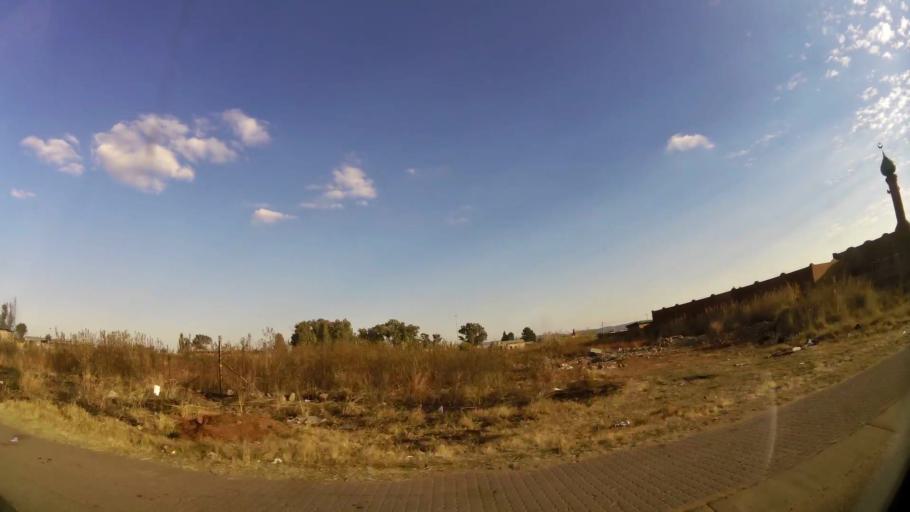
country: ZA
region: Gauteng
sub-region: City of Tshwane Metropolitan Municipality
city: Cullinan
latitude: -25.7091
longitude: 28.3751
